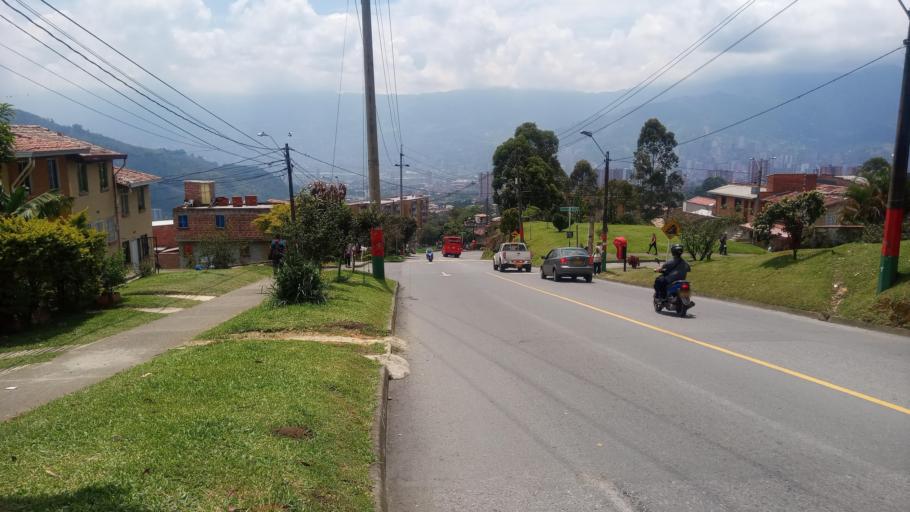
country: CO
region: Antioquia
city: La Estrella
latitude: 6.1738
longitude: -75.6502
